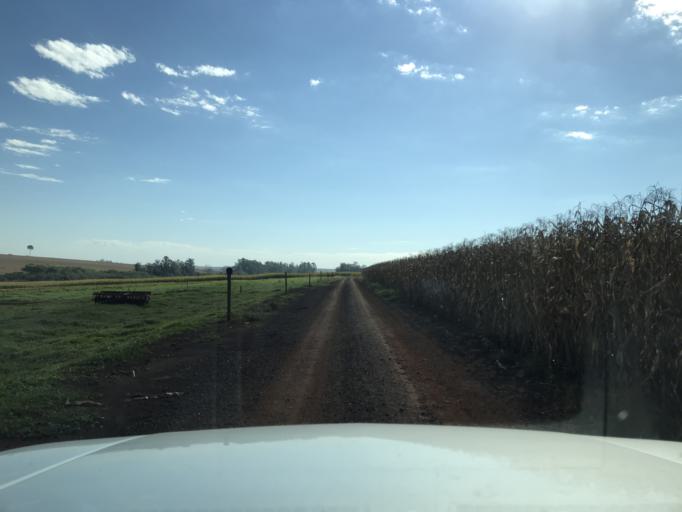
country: BR
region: Parana
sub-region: Palotina
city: Palotina
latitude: -24.2658
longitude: -53.8145
